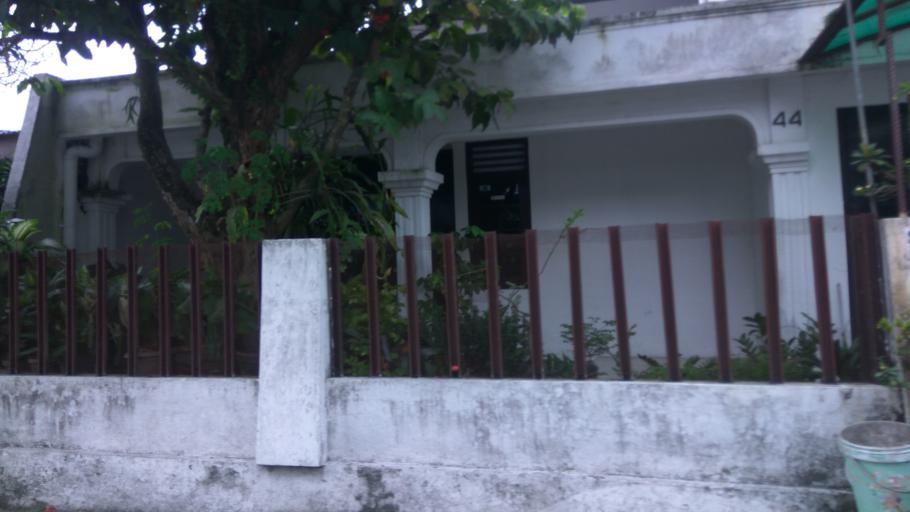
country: ID
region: Daerah Istimewa Yogyakarta
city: Depok
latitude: -7.7397
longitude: 110.4086
